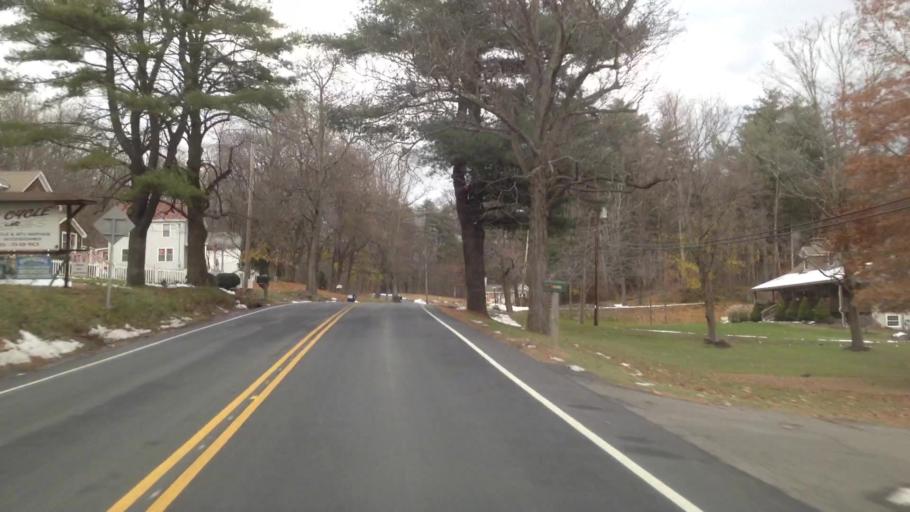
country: US
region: New York
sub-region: Ulster County
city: Lake Katrine
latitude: 42.0063
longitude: -73.9663
